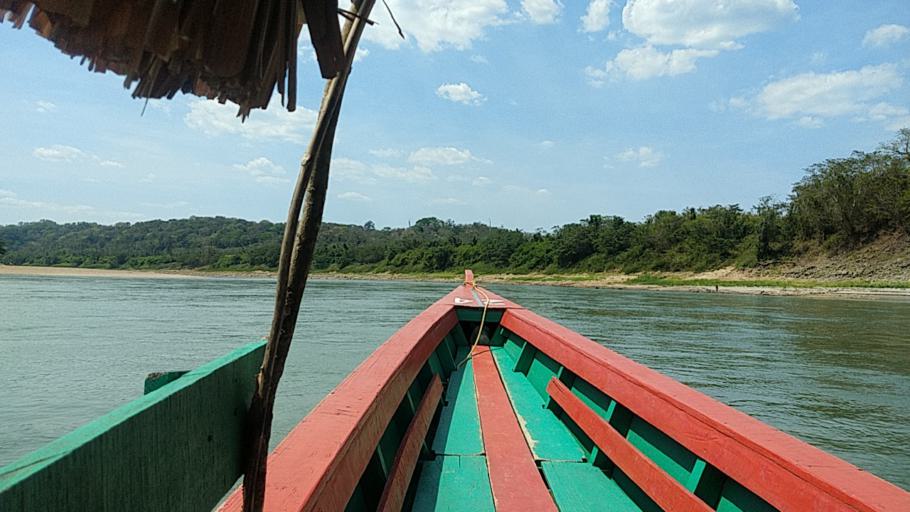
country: MX
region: Chiapas
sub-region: Ocosingo
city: Frontera Corozal
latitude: 16.8943
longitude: -90.9563
